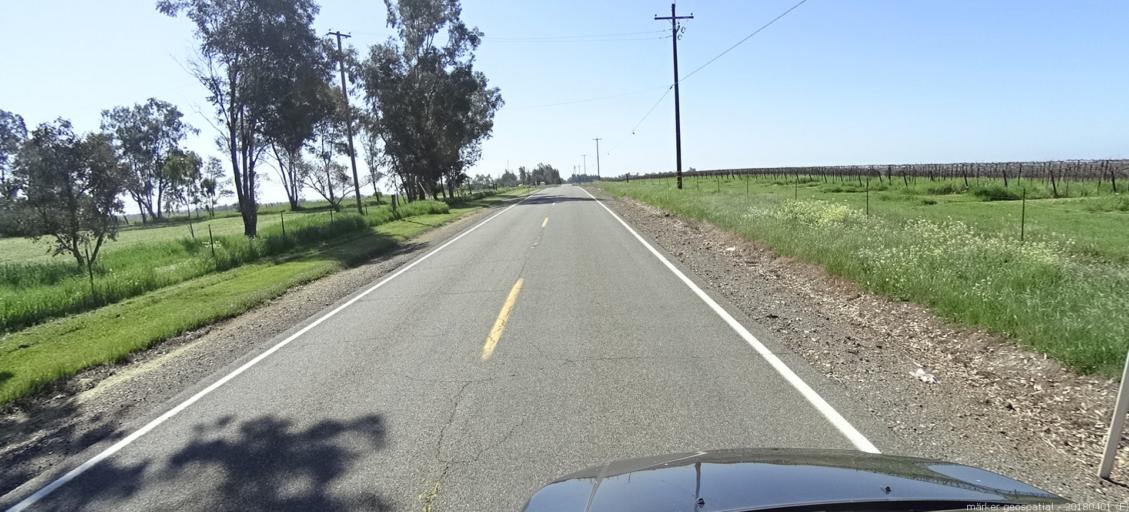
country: US
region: California
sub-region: Sacramento County
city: Wilton
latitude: 38.3740
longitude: -121.2239
